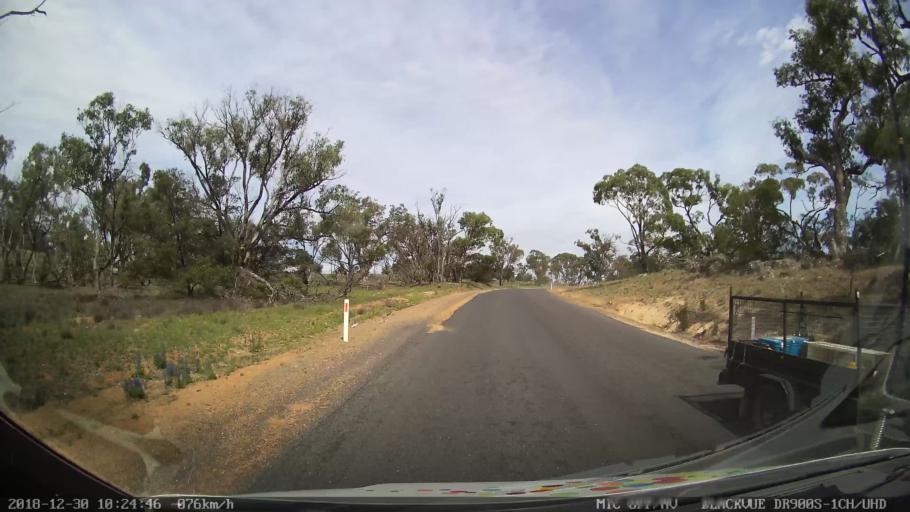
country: AU
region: New South Wales
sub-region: Snowy River
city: Berridale
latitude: -36.5309
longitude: 148.9642
